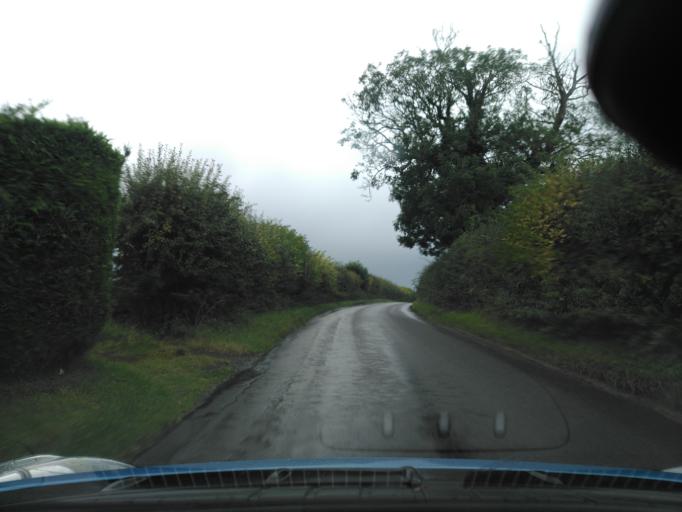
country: GB
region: England
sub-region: Borough of Swindon
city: Wanborough
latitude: 51.5473
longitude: -1.6736
